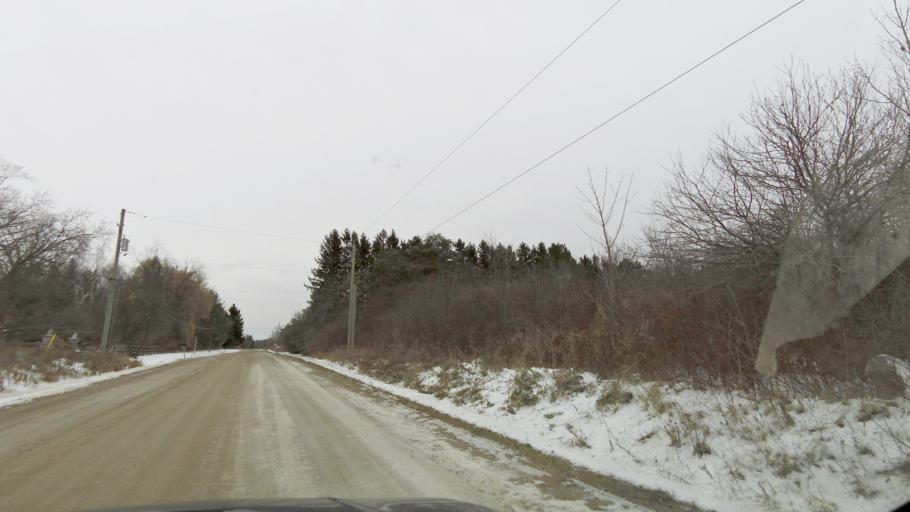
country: CA
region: Ontario
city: Vaughan
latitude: 43.9406
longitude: -79.6103
